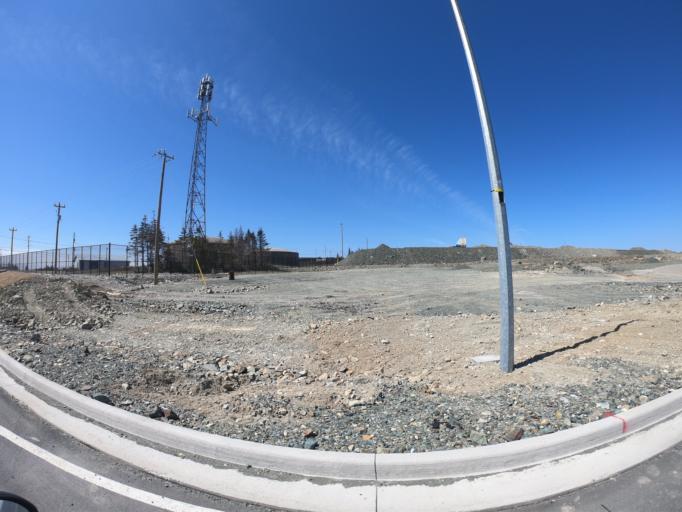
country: CA
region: Newfoundland and Labrador
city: Mount Pearl
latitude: 47.5078
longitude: -52.8297
